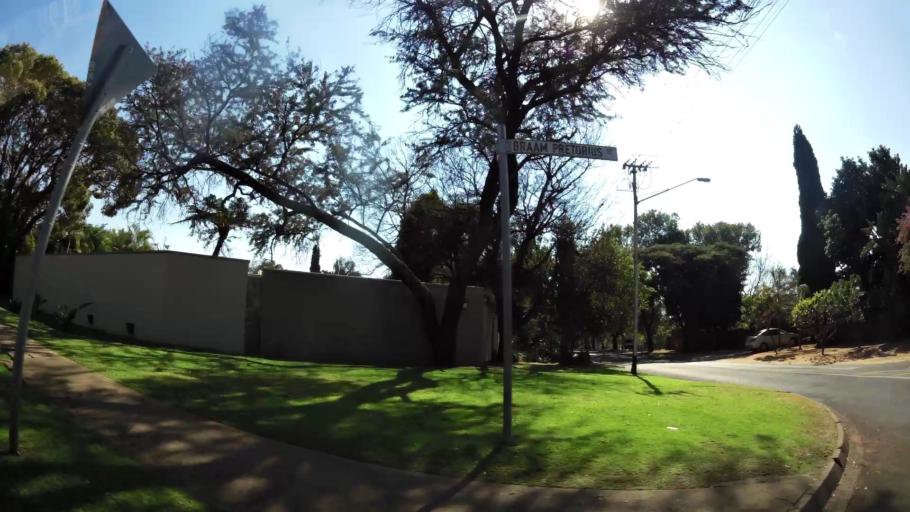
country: ZA
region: Gauteng
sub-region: City of Tshwane Metropolitan Municipality
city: Pretoria
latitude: -25.6866
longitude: 28.2252
